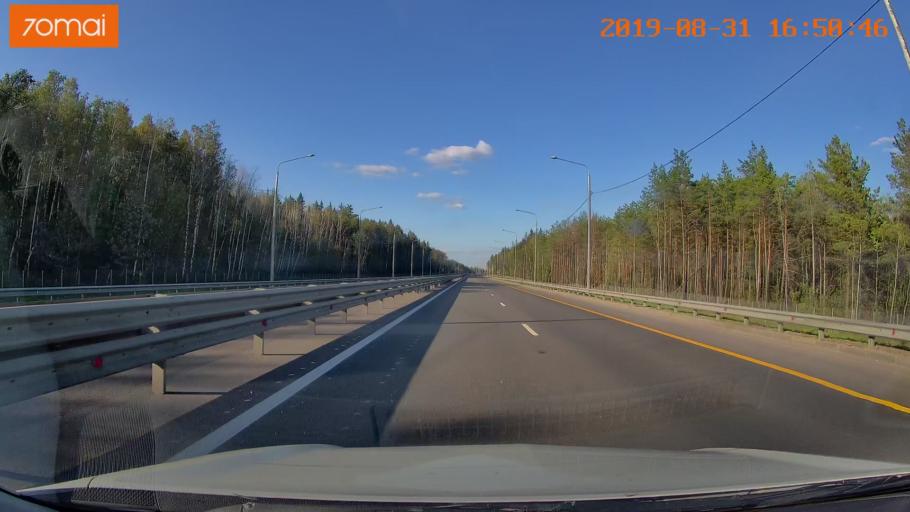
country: RU
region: Kaluga
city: Pyatovskiy
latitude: 54.7145
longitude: 36.1652
